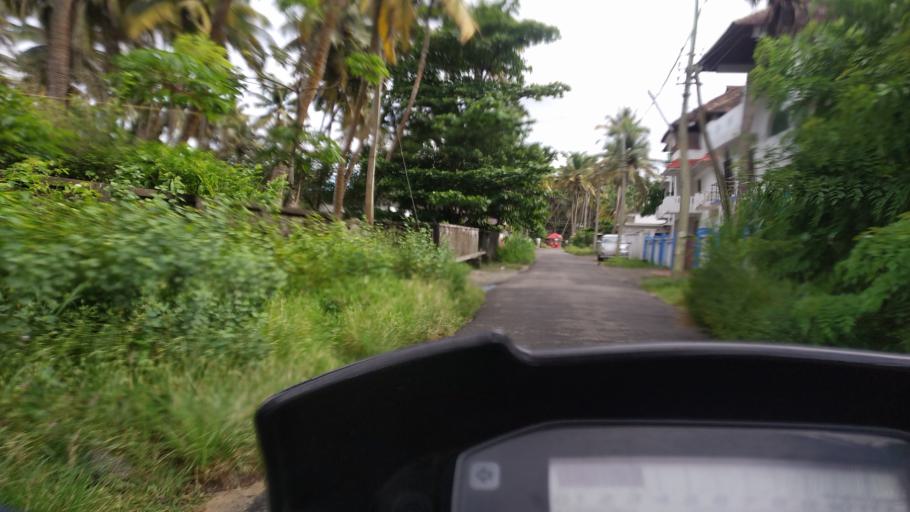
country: IN
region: Kerala
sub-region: Thrissur District
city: Kodungallur
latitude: 10.1608
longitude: 76.1718
